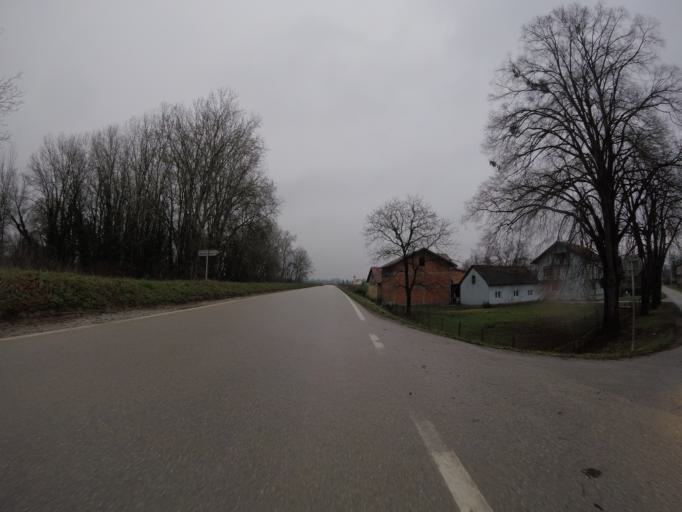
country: HR
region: Zagrebacka
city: Kuce
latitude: 45.6906
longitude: 16.2320
